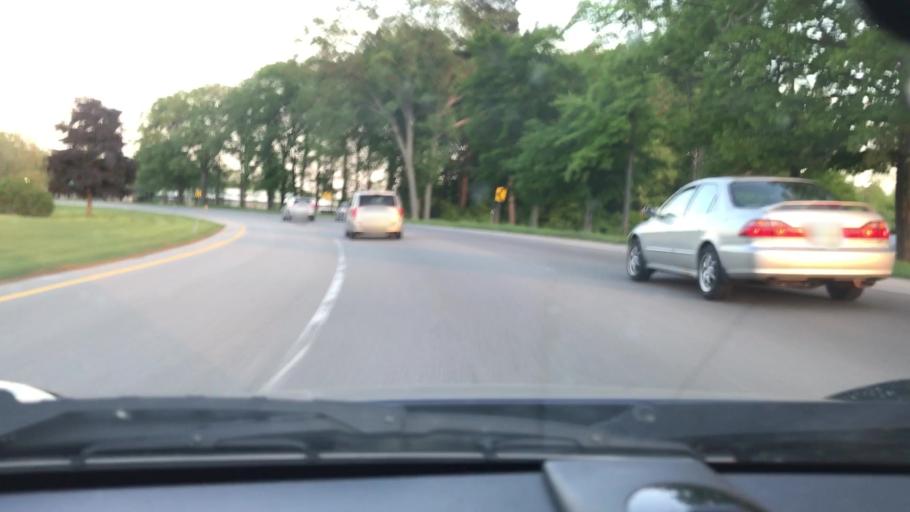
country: US
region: Michigan
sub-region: Muskegon County
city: Roosevelt Park
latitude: 43.1902
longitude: -86.2595
